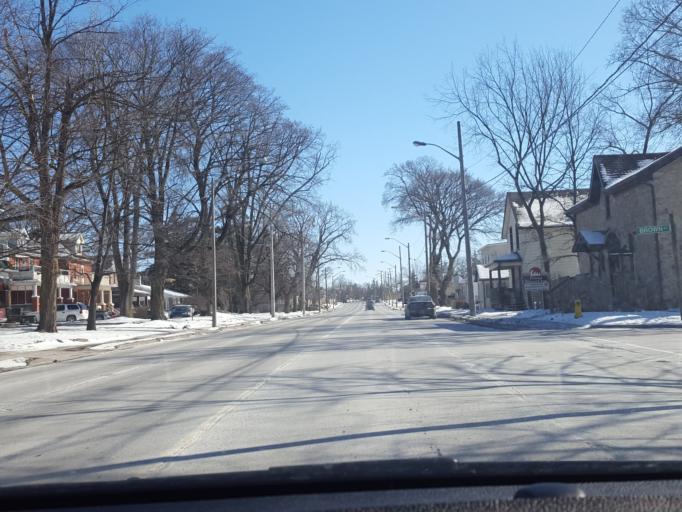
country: CA
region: Ontario
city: Cambridge
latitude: 43.3893
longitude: -80.3455
